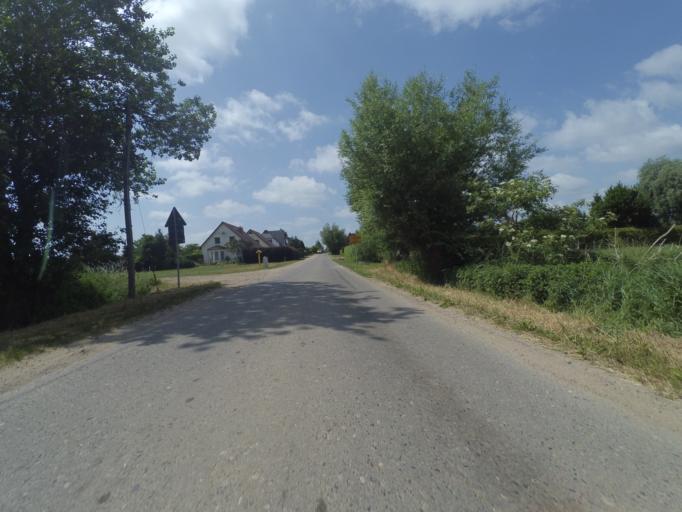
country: DE
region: Mecklenburg-Vorpommern
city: Lubz
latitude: 53.4531
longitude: 12.0010
